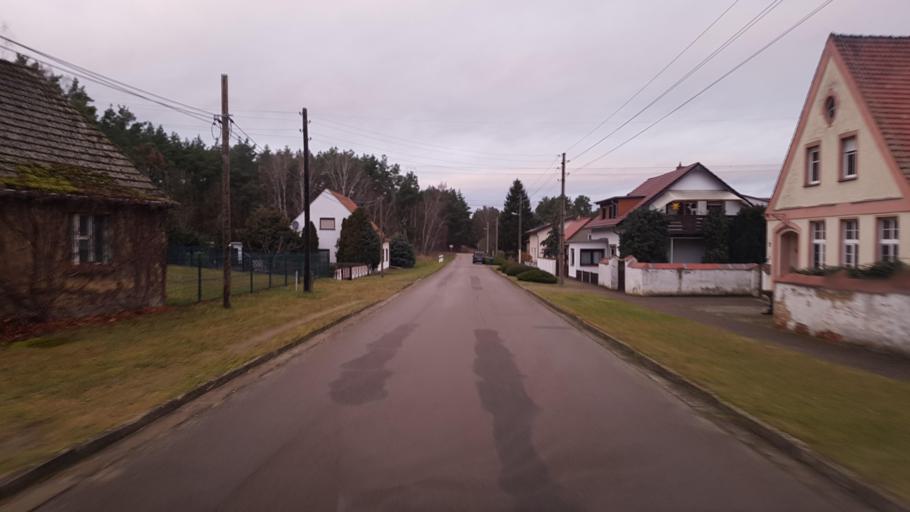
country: DE
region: Brandenburg
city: Luebben
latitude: 51.9084
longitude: 13.8065
